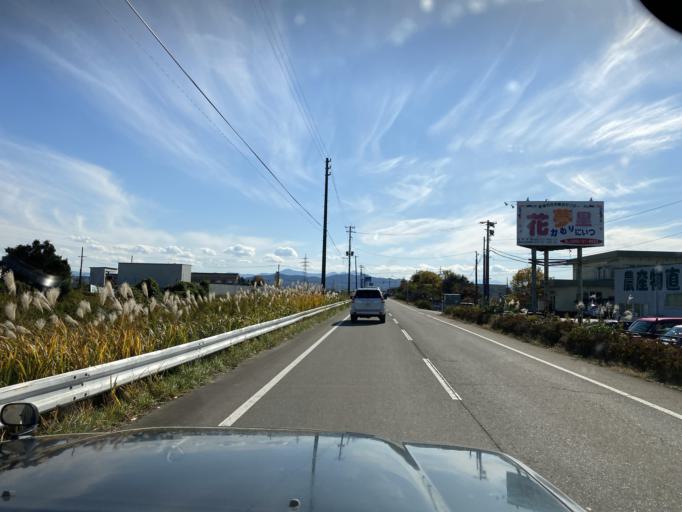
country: JP
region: Niigata
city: Niitsu-honcho
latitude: 37.7928
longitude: 139.0795
